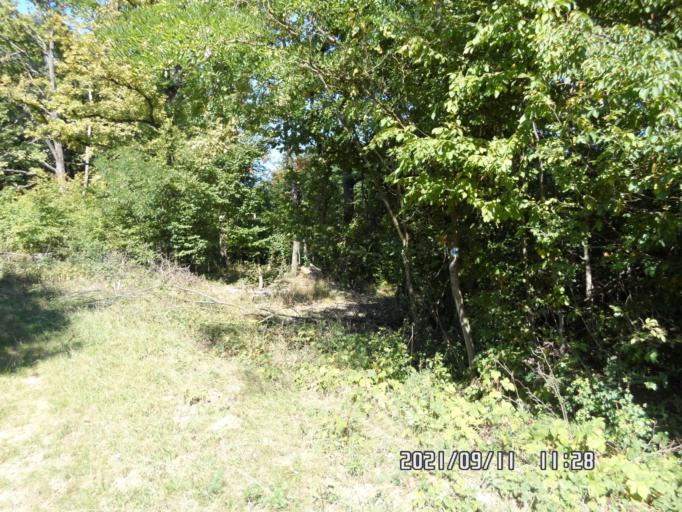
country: HU
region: Zala
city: Zalalovo
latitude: 46.7348
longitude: 16.7057
